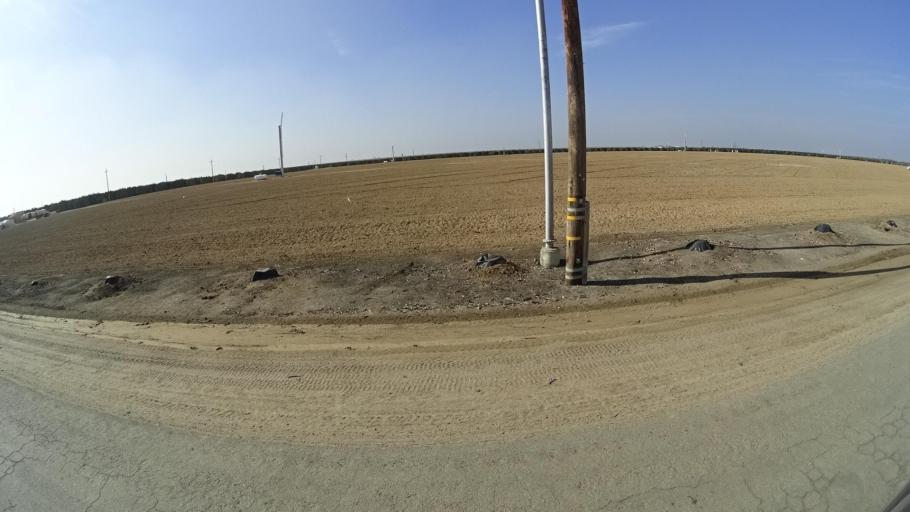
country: US
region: California
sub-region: Kern County
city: Shafter
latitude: 35.5379
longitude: -119.1337
